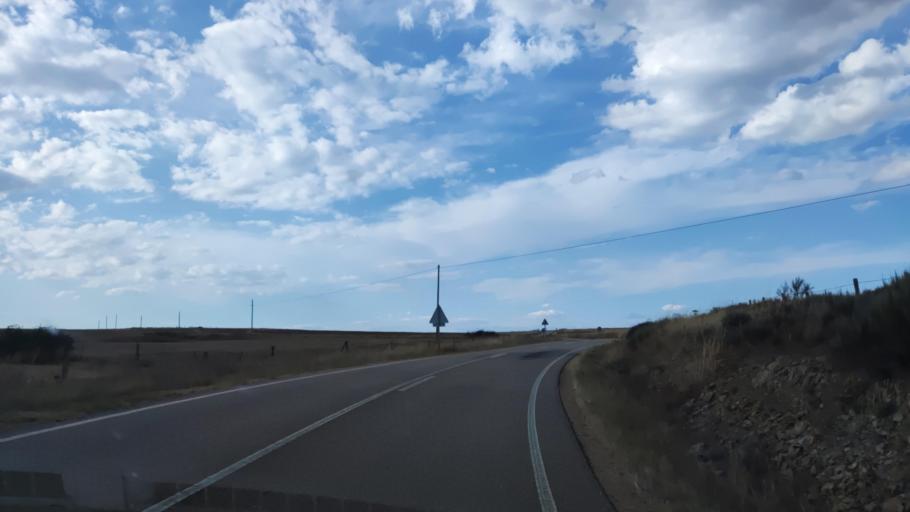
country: ES
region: Castille and Leon
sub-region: Provincia de Salamanca
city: Pastores
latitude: 40.5060
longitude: -6.5041
